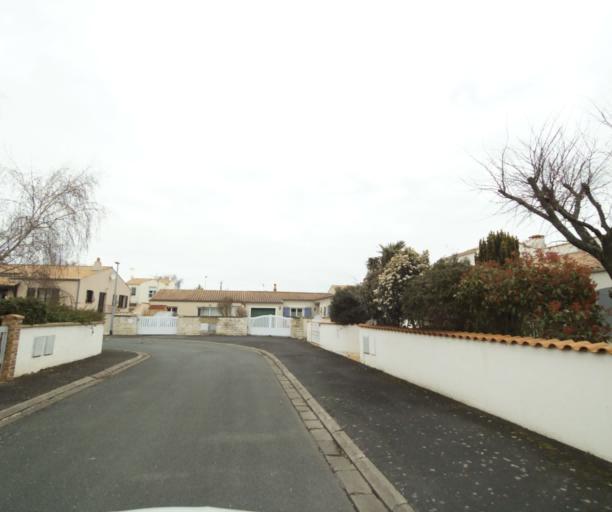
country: FR
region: Poitou-Charentes
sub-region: Departement de la Charente-Maritime
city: Lagord
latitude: 46.1925
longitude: -1.1550
